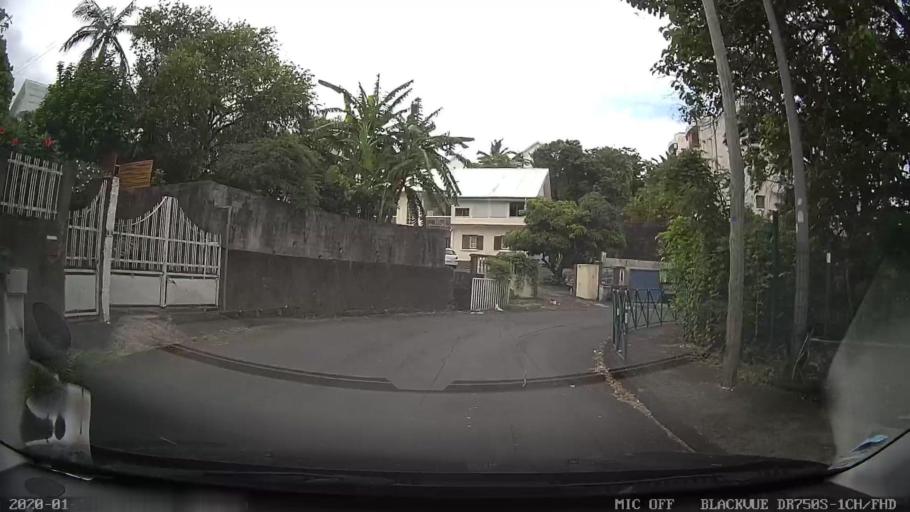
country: RE
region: Reunion
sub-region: Reunion
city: Saint-Denis
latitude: -20.9125
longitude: 55.4858
